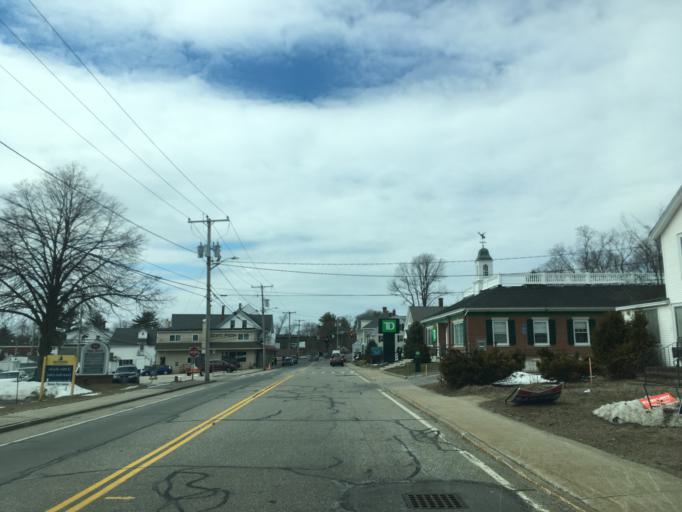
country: US
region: New Hampshire
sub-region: Rockingham County
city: Hampton
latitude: 42.9412
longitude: -70.8360
